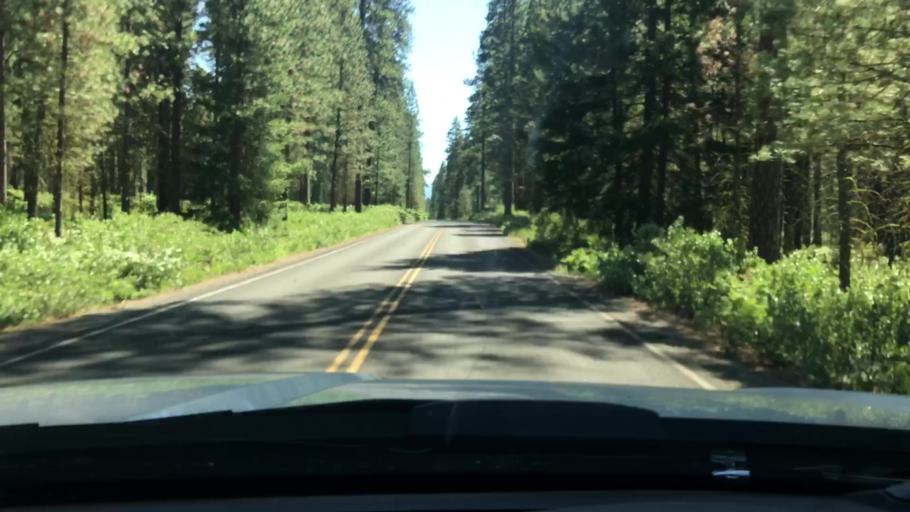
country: US
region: Oregon
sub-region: Deschutes County
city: Sisters
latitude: 44.4203
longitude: -121.6686
